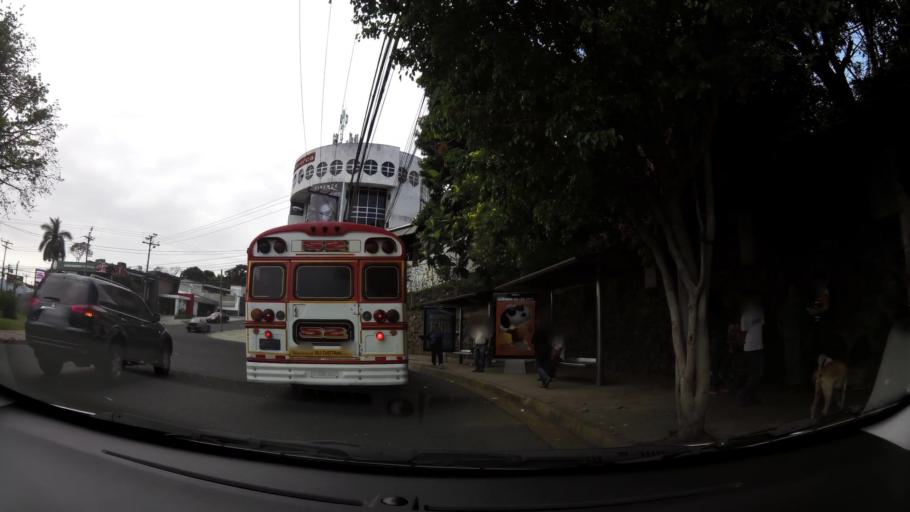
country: SV
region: San Salvador
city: Mejicanos
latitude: 13.7122
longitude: -89.2479
